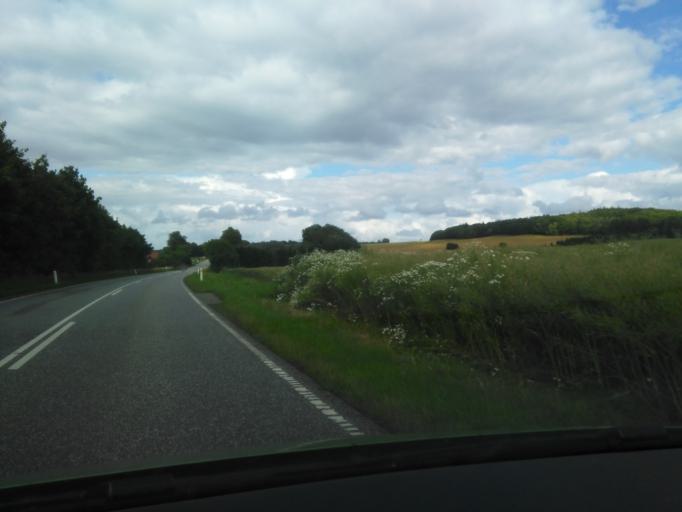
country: DK
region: Central Jutland
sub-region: Skanderborg Kommune
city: Ry
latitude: 56.0052
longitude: 9.7756
